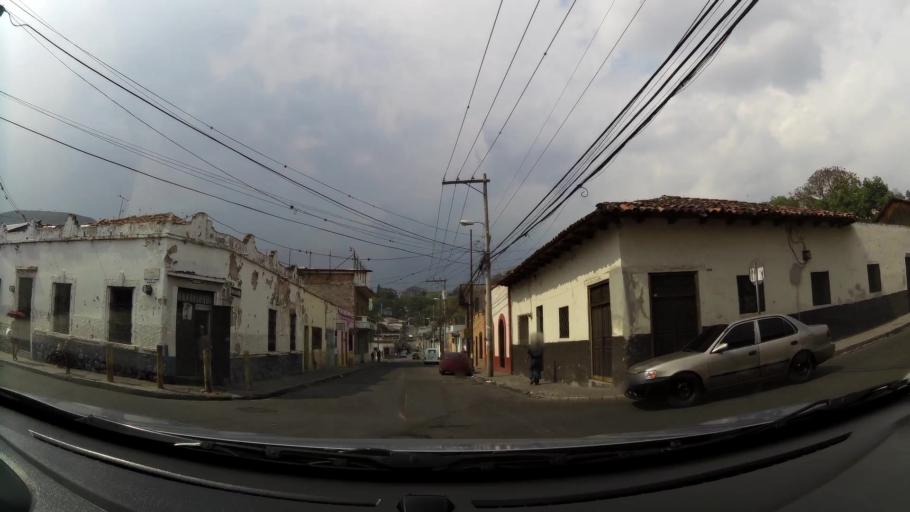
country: HN
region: Francisco Morazan
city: Tegucigalpa
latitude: 14.1099
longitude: -87.2079
